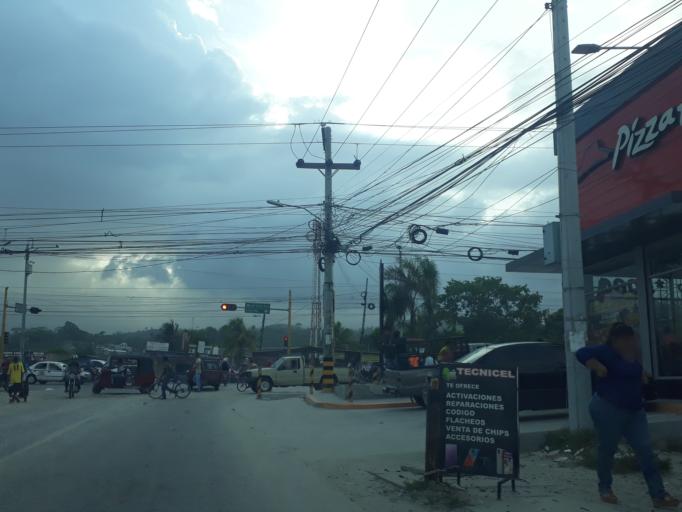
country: HN
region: Cortes
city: Choloma
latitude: 15.5733
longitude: -87.9533
